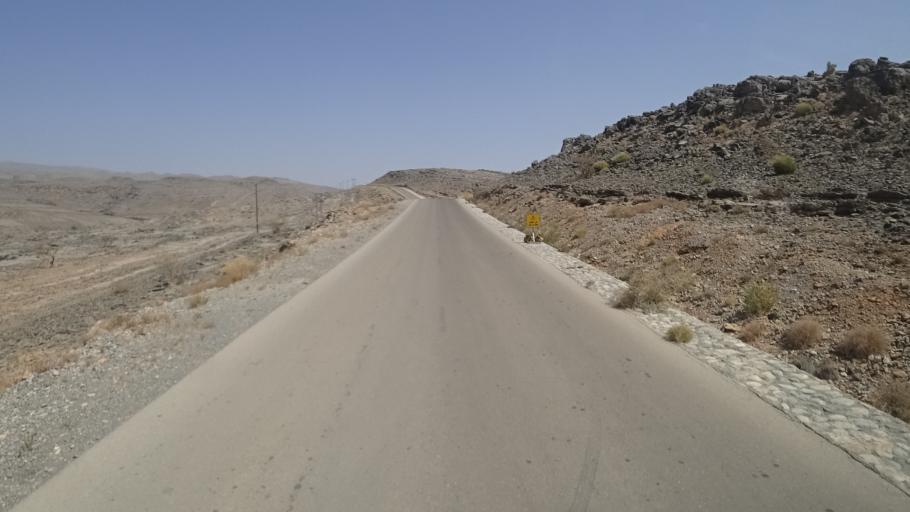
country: OM
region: Muhafazat ad Dakhiliyah
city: Bahla'
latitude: 23.0993
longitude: 57.3718
